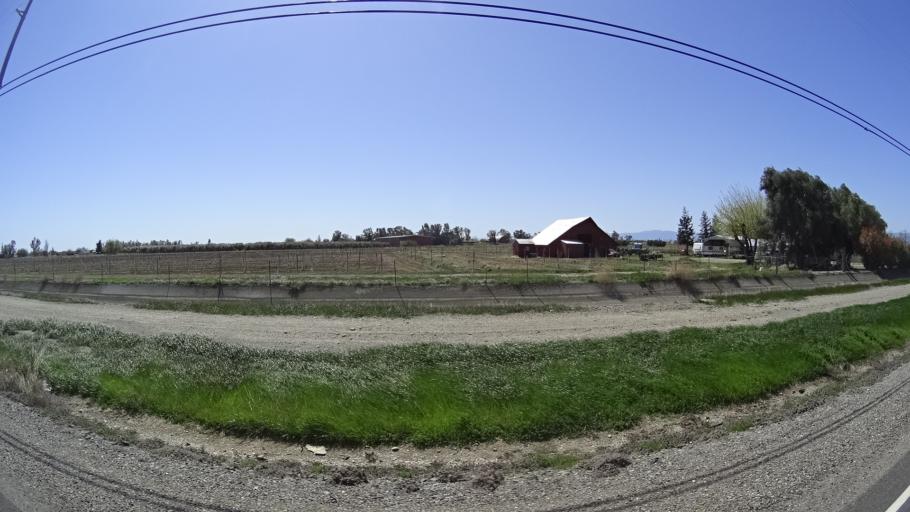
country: US
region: California
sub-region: Glenn County
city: Orland
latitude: 39.7647
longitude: -122.2419
